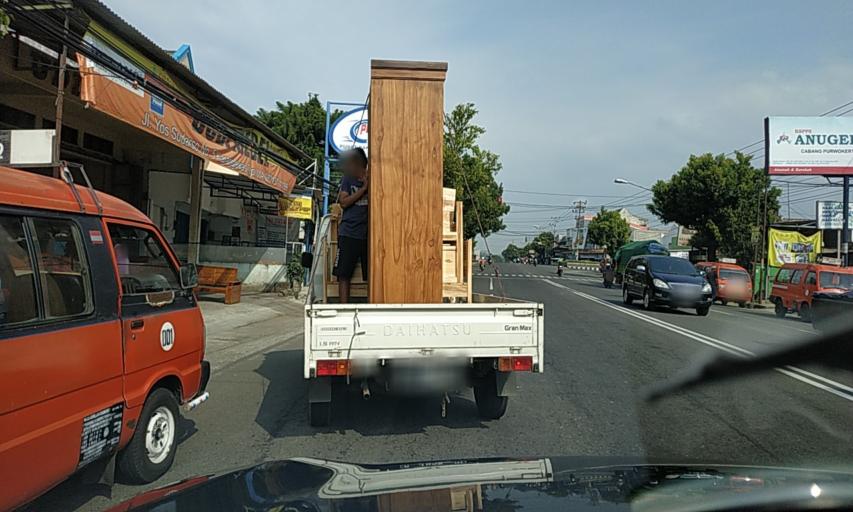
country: ID
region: Central Java
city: Purwokerto
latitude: -7.4207
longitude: 109.2012
